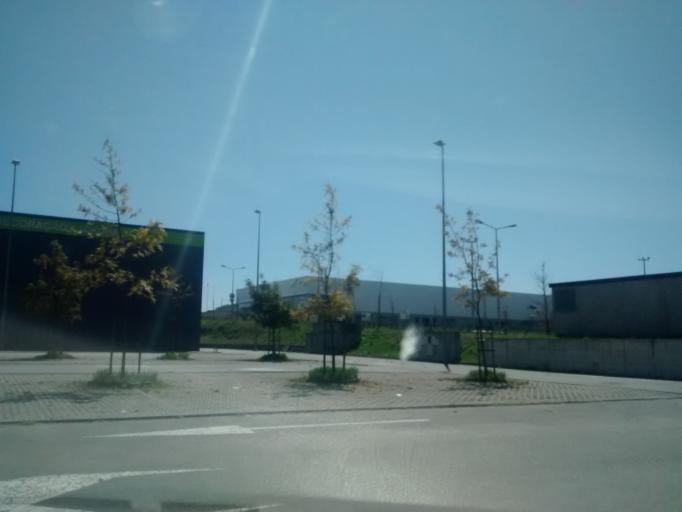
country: PT
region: Braga
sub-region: Guimaraes
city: Candoso
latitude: 41.4401
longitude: -8.3348
